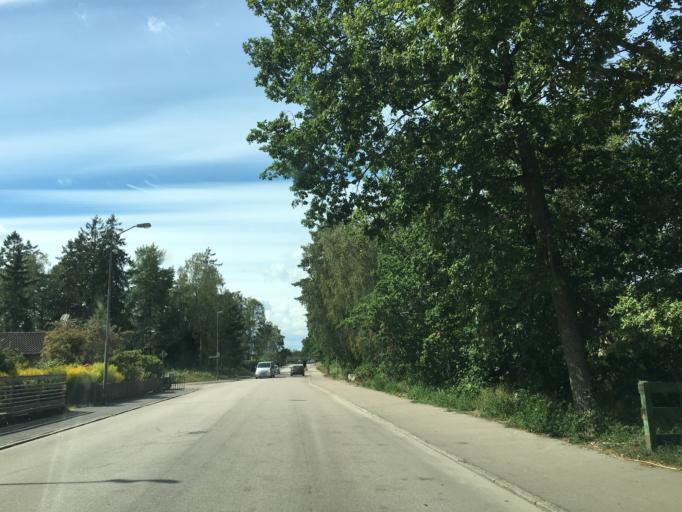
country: SE
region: Kalmar
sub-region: Kalmar Kommun
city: Kalmar
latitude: 56.6991
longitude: 16.3563
